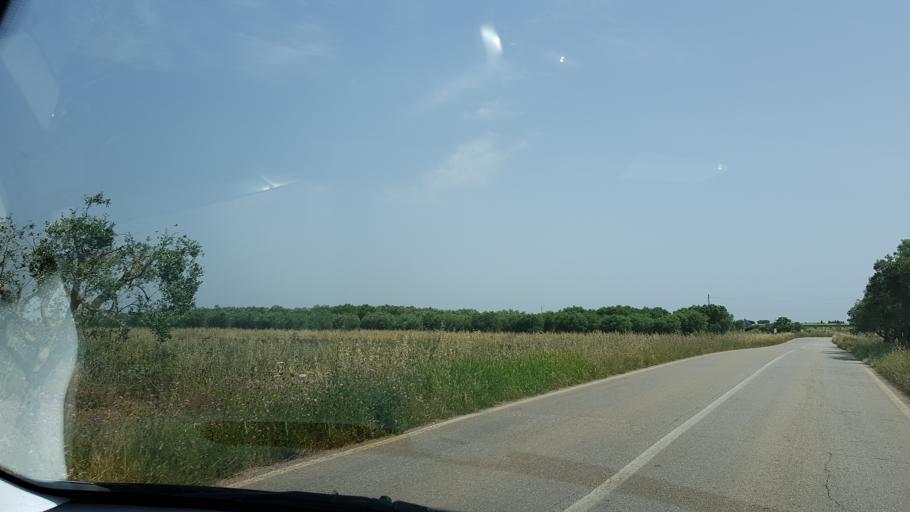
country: IT
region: Apulia
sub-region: Provincia di Brindisi
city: San Pancrazio Salentino
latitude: 40.4433
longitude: 17.8410
